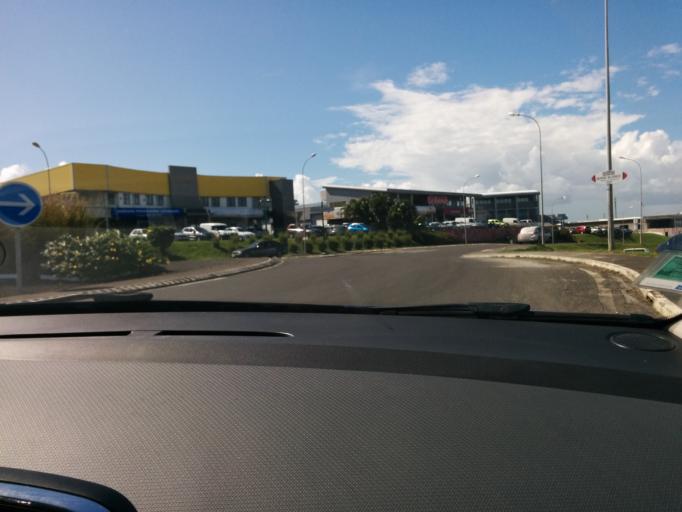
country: GP
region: Guadeloupe
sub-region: Guadeloupe
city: Baie-Mahault
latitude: 16.2386
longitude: -61.5698
